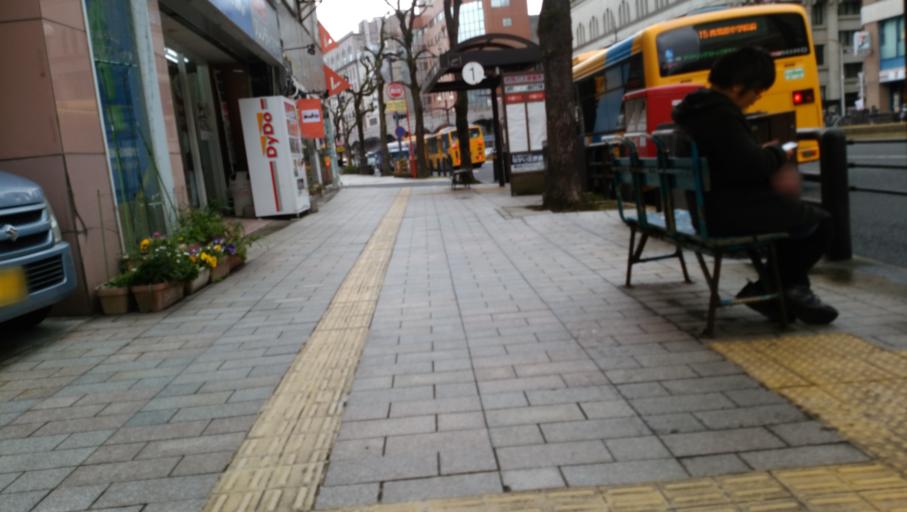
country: JP
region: Kagoshima
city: Kagoshima-shi
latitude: 31.5954
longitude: 130.5574
